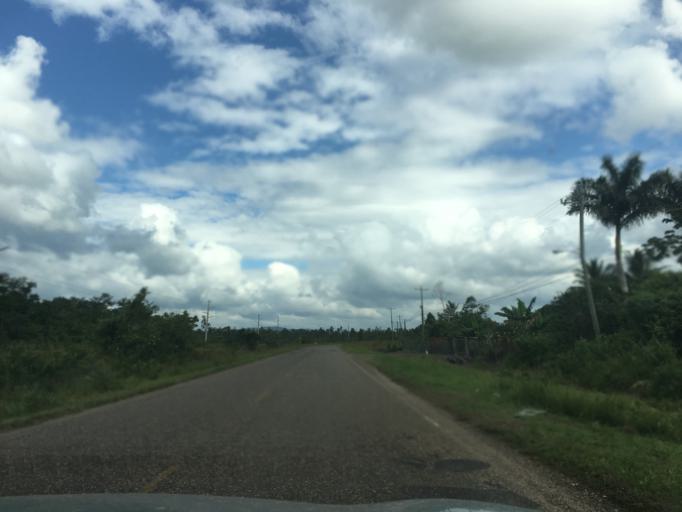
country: BZ
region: Stann Creek
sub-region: Dangriga
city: Dangriga
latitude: 16.8676
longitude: -88.3479
